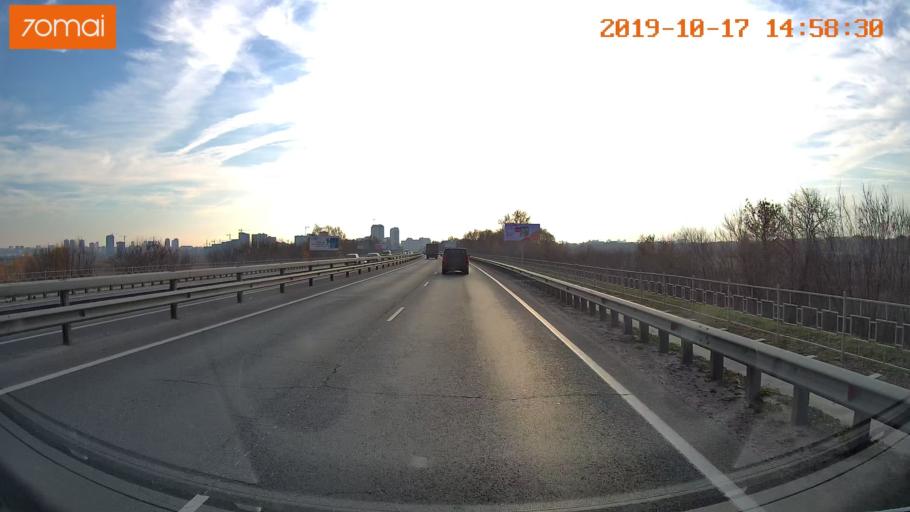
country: RU
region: Rjazan
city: Polyany
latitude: 54.6461
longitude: 39.7889
